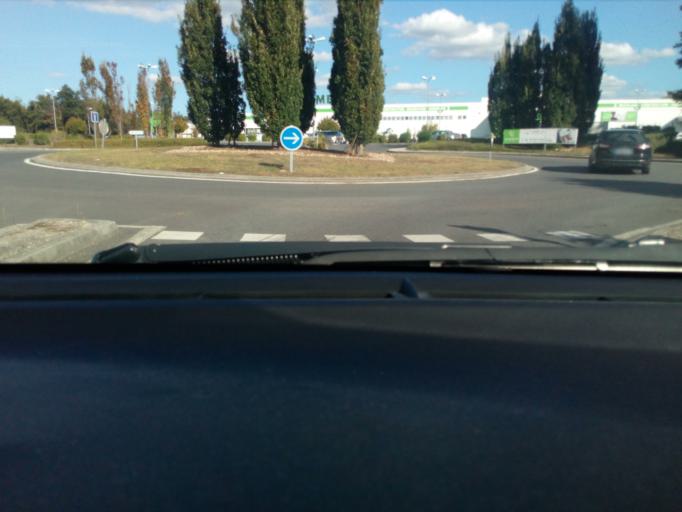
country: FR
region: Poitou-Charentes
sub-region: Departement de la Charente
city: Soyaux
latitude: 45.6339
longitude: 0.2145
